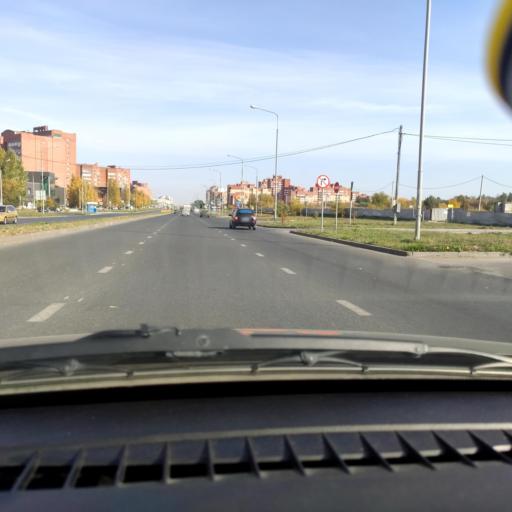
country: RU
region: Samara
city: Tol'yatti
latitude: 53.5327
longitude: 49.3448
